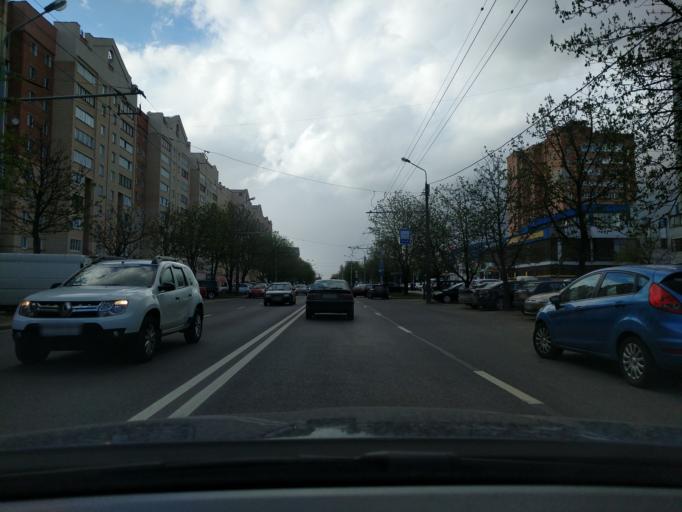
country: BY
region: Minsk
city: Novoye Medvezhino
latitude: 53.9050
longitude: 27.4813
